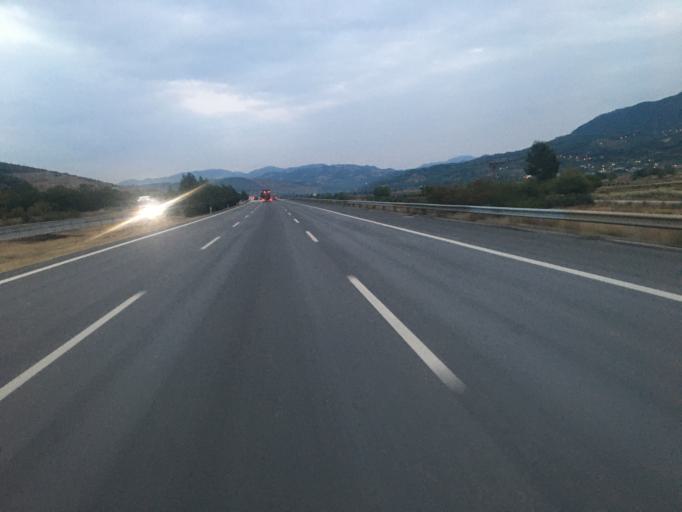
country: TR
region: Osmaniye
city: Osmaniye
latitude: 37.1481
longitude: 36.3388
